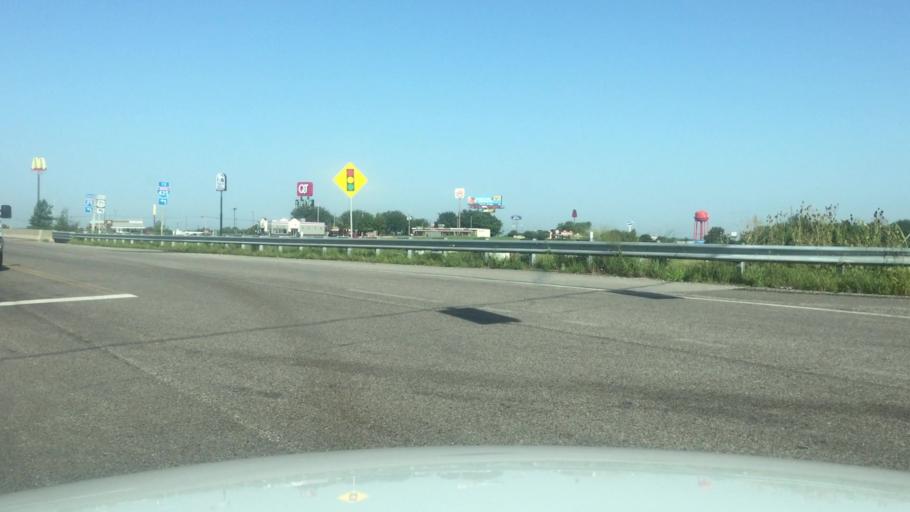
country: US
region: Missouri
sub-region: Platte County
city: Platte City
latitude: 39.3539
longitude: -94.7606
